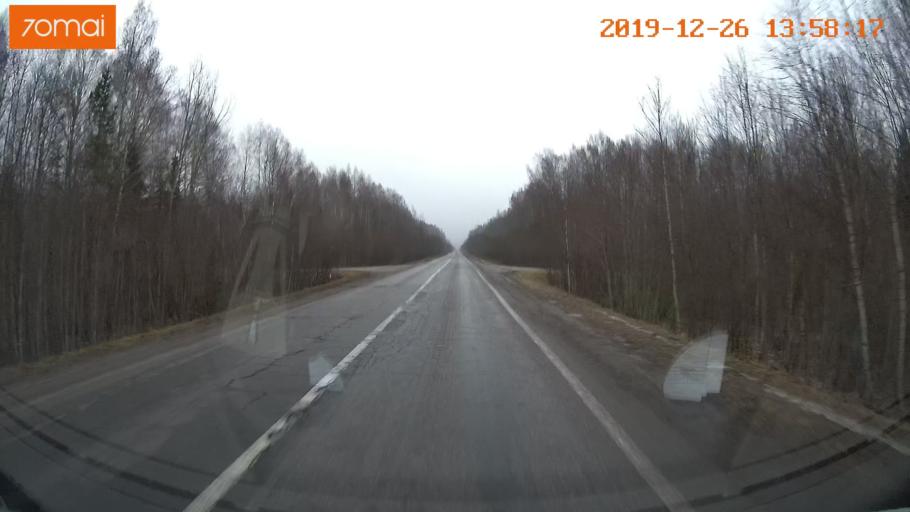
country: RU
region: Jaroslavl
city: Poshekhon'ye
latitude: 58.5754
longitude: 38.6973
